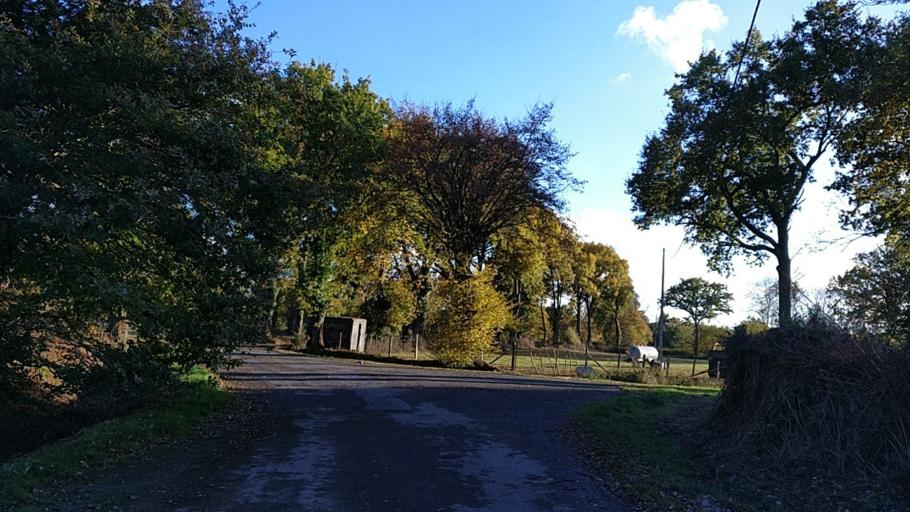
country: FR
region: Brittany
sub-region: Departement d'Ille-et-Vilaine
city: Fouillard
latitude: 48.1308
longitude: -1.5674
